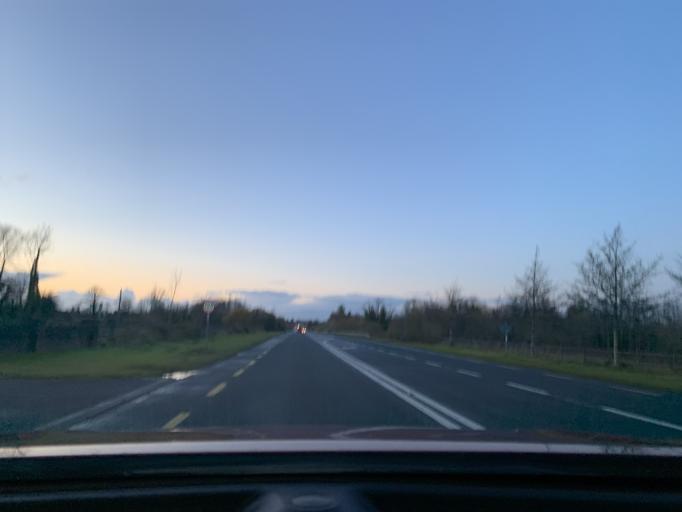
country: IE
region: Connaught
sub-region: County Leitrim
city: Carrick-on-Shannon
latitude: 53.9379
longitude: -8.0583
